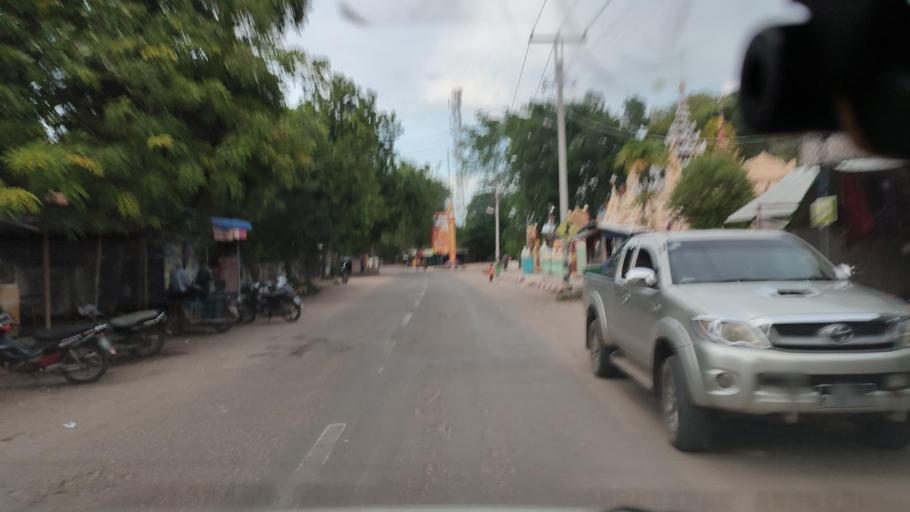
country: MM
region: Magway
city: Minbu
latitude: 20.2270
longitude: 94.7637
